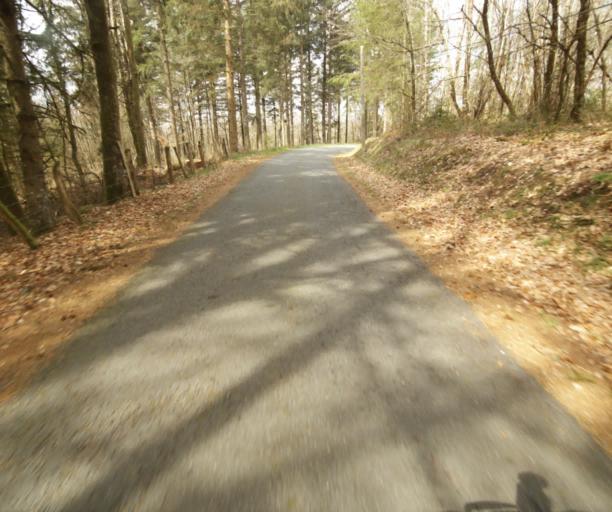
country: FR
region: Limousin
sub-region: Departement de la Correze
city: Correze
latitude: 45.3864
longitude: 1.9194
